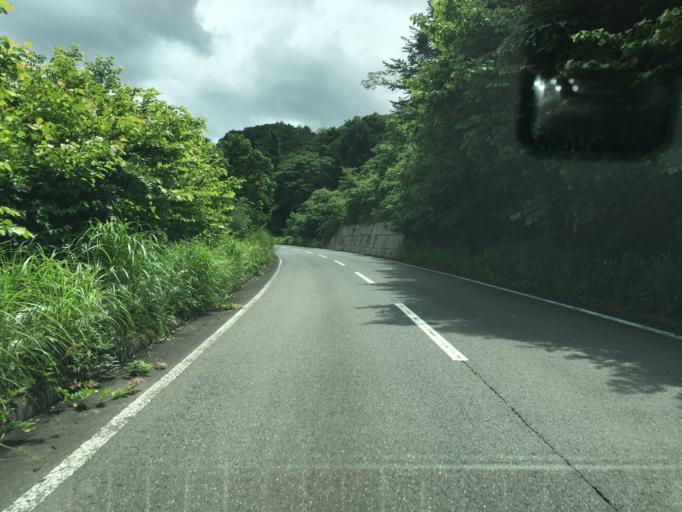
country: JP
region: Miyagi
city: Marumori
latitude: 37.7086
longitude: 140.8776
